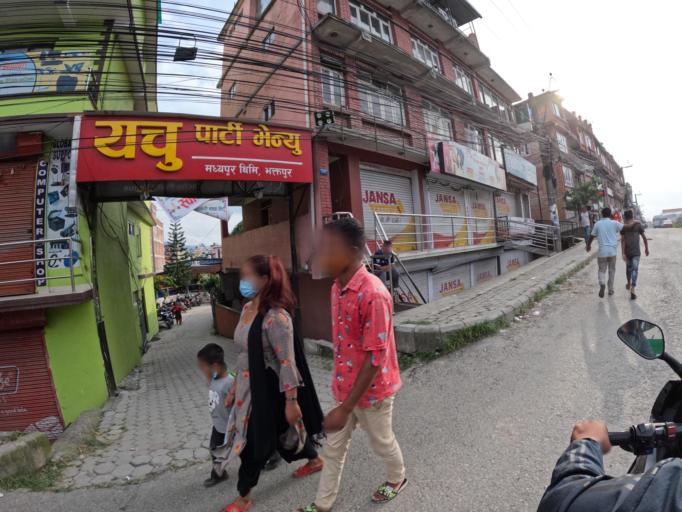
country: NP
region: Central Region
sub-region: Bagmati Zone
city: Bhaktapur
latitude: 27.6731
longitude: 85.3838
